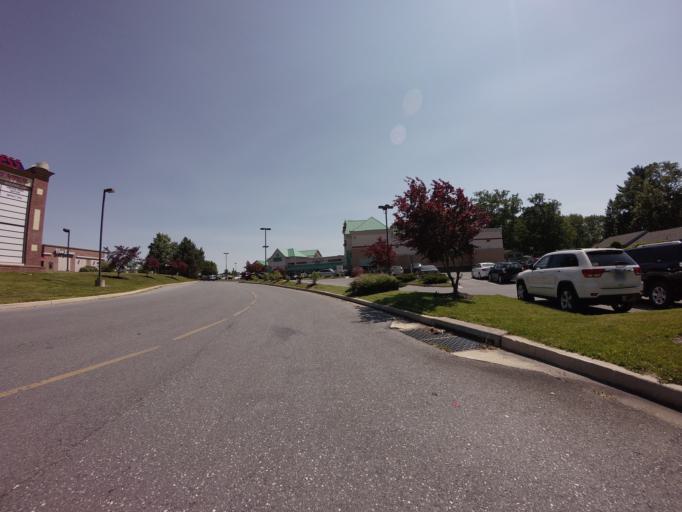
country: US
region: Maryland
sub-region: Carroll County
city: Eldersburg
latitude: 39.4047
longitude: -76.9536
